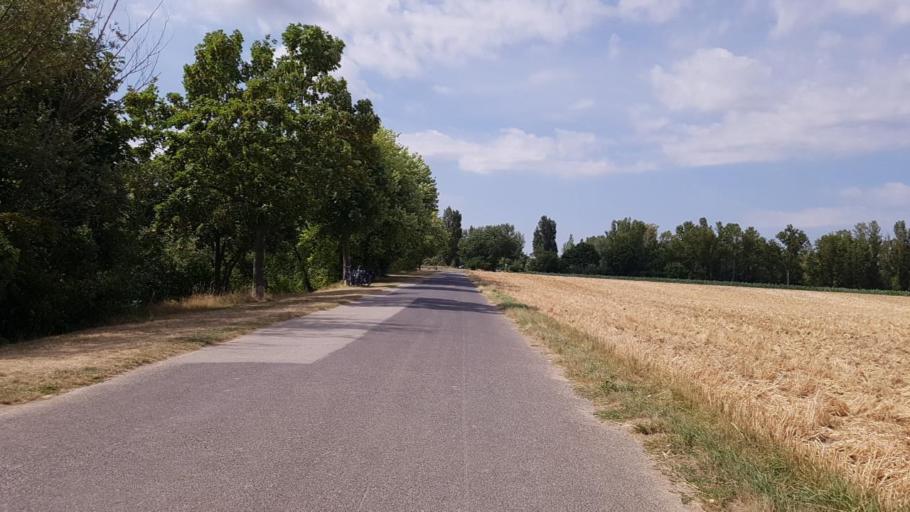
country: DE
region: Rheinland-Pfalz
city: Gartenstadt
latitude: 49.5012
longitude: 8.3855
